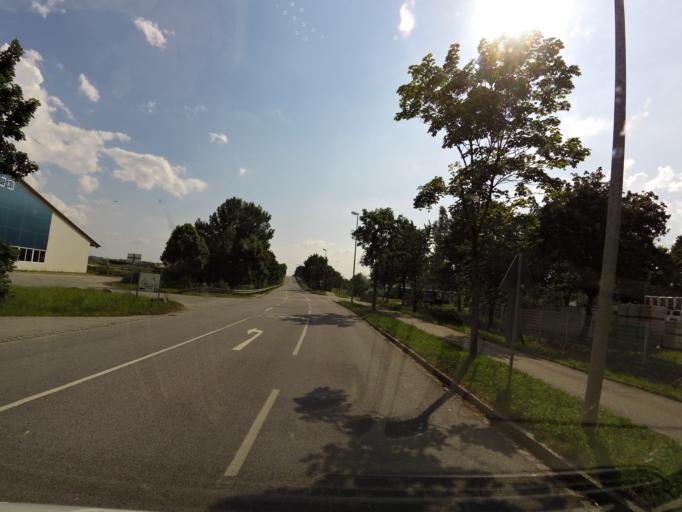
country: DE
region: Bavaria
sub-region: Lower Bavaria
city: Hengersberg
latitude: 48.7661
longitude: 13.0592
